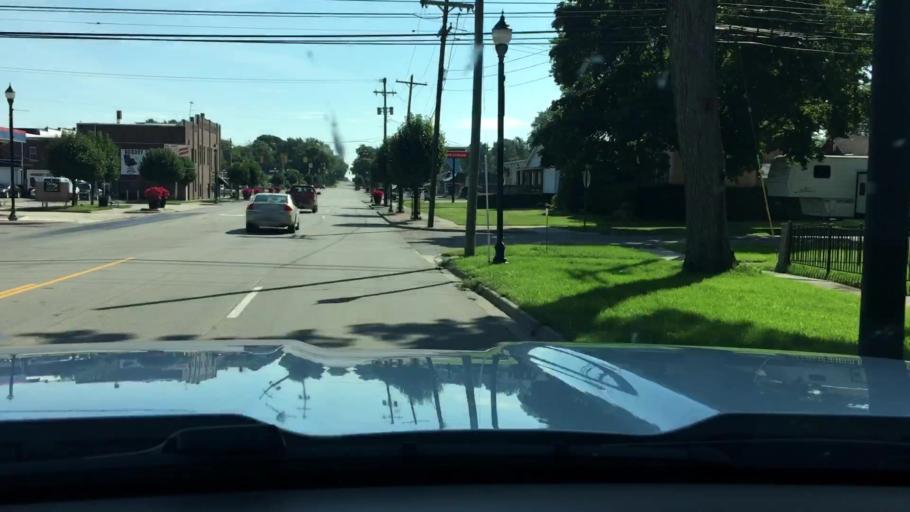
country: US
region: Michigan
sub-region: Gratiot County
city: Saint Louis
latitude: 43.4078
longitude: -84.6106
